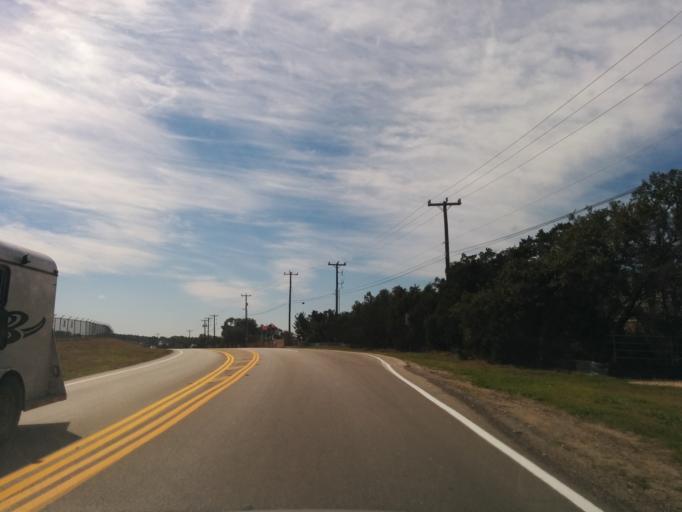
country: US
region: Texas
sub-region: Bexar County
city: Fair Oaks Ranch
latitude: 29.7070
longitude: -98.6297
